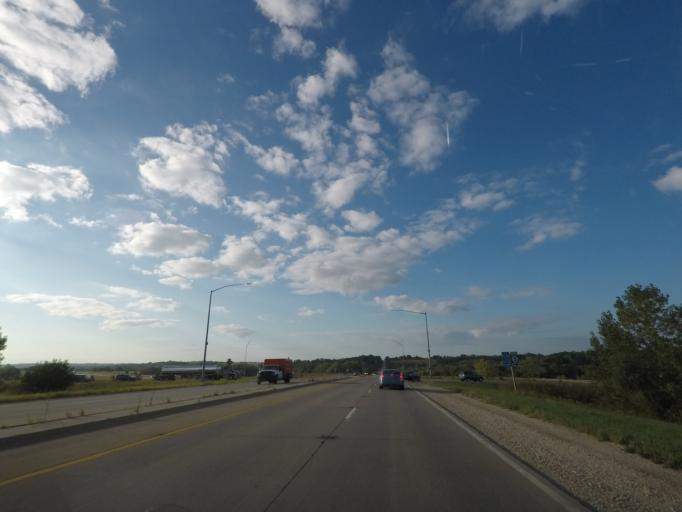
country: US
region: Iowa
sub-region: Warren County
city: Norwalk
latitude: 41.5099
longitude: -93.6451
